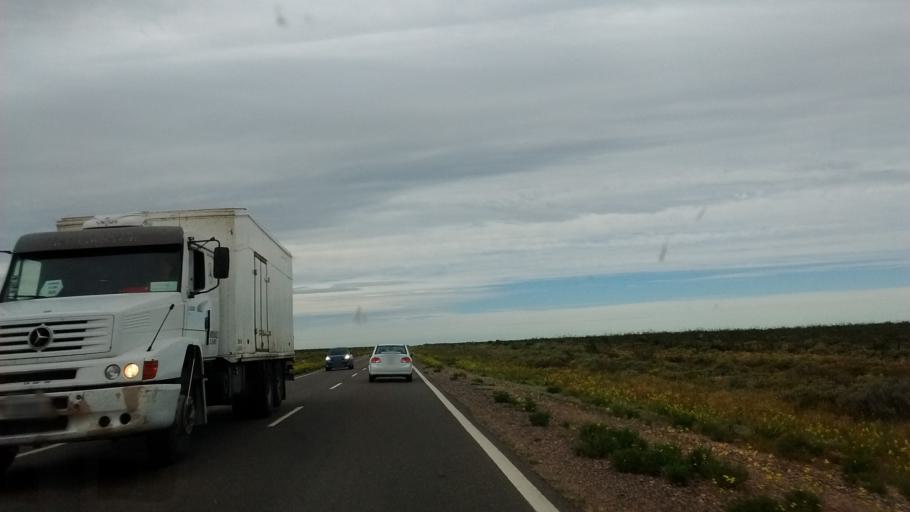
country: AR
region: Rio Negro
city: Contraalmirante Cordero
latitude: -38.3334
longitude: -68.0093
